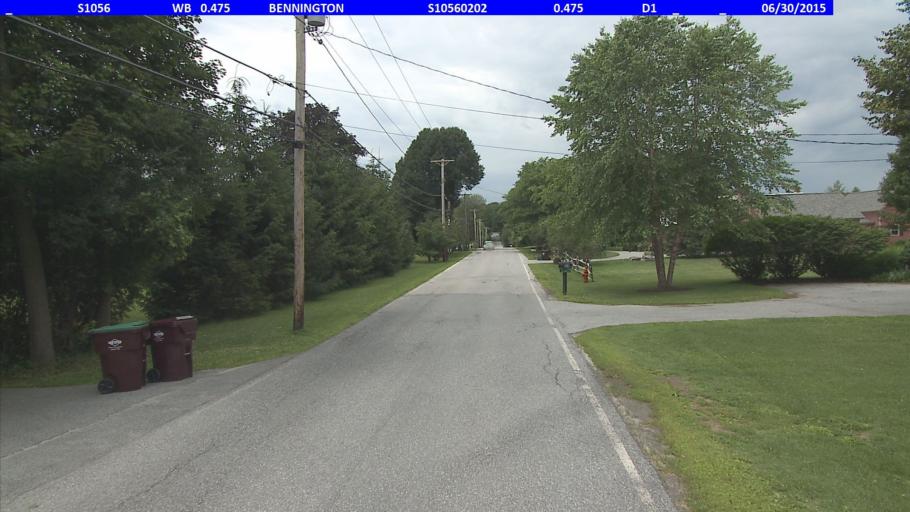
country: US
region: Vermont
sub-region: Bennington County
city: Bennington
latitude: 42.8879
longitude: -73.2201
